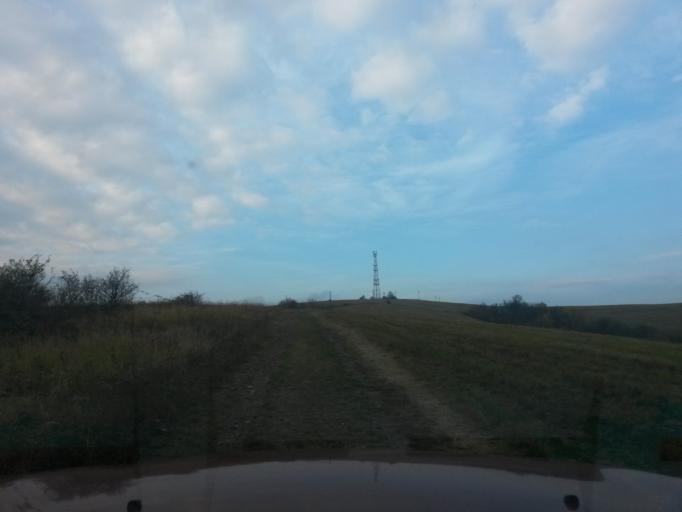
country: SK
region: Kosicky
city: Kosice
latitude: 48.7635
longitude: 21.2111
